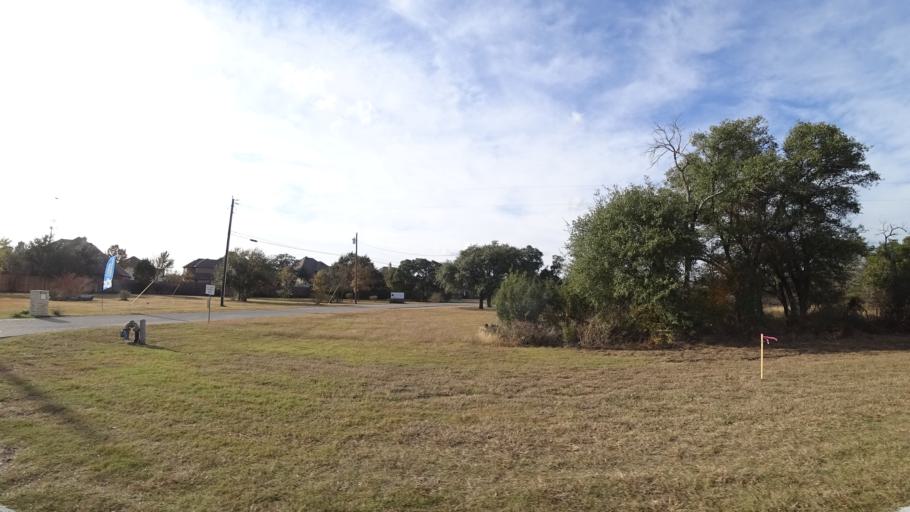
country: US
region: Texas
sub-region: Williamson County
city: Brushy Creek
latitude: 30.5068
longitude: -97.7187
